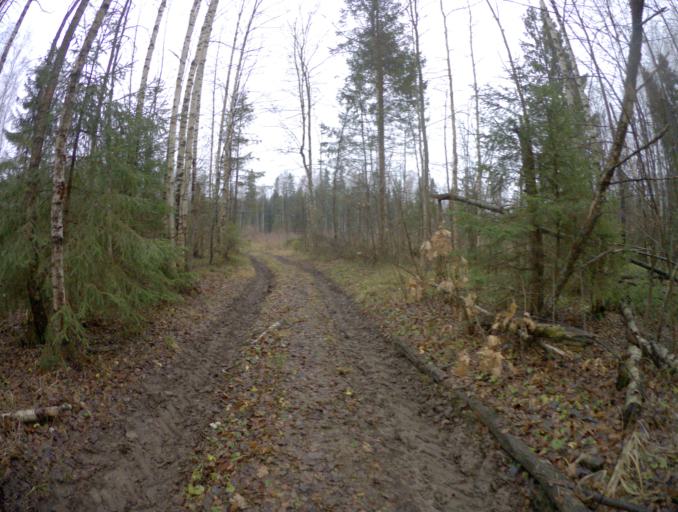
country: RU
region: Vladimir
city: Golovino
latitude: 56.0011
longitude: 40.4716
